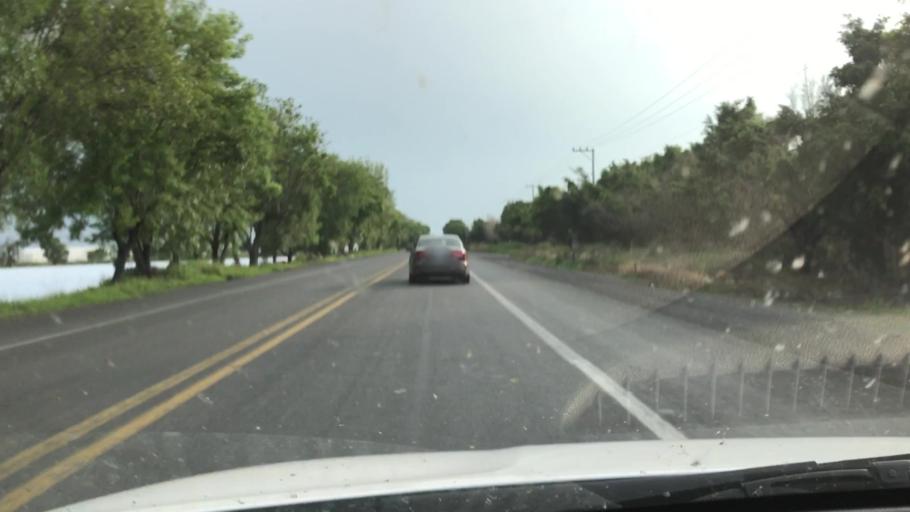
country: MX
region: Michoacan
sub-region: Yurecuaro
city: Yurecuaro
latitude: 20.3203
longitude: -102.2926
